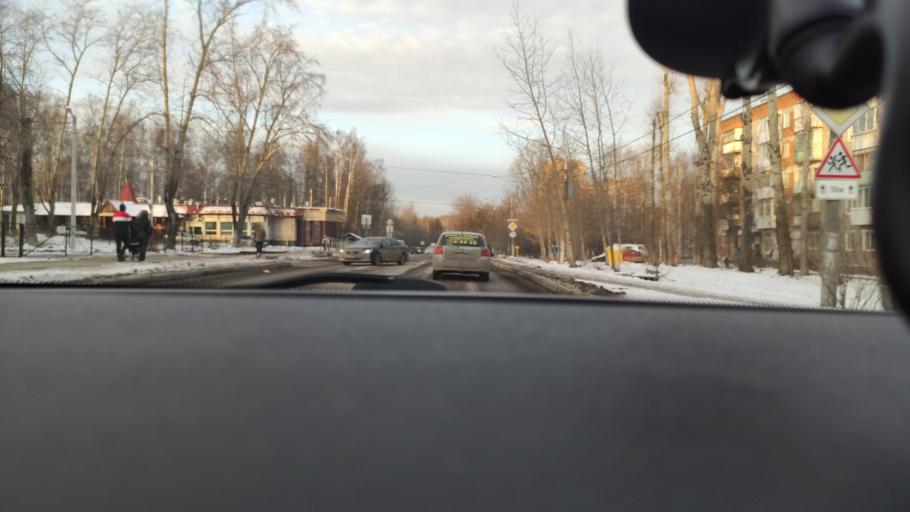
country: RU
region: Perm
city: Perm
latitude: 58.1115
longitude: 56.3039
